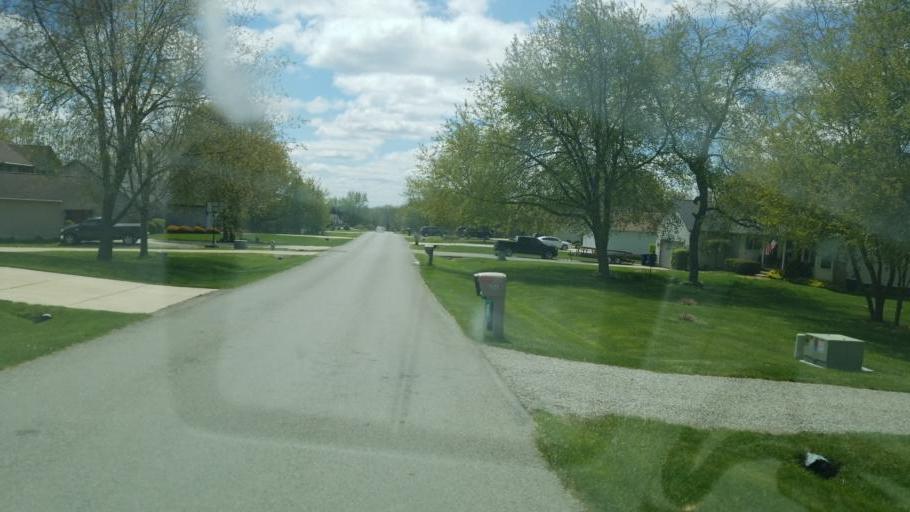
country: US
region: Ohio
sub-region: Knox County
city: Gambier
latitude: 40.4437
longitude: -82.3639
